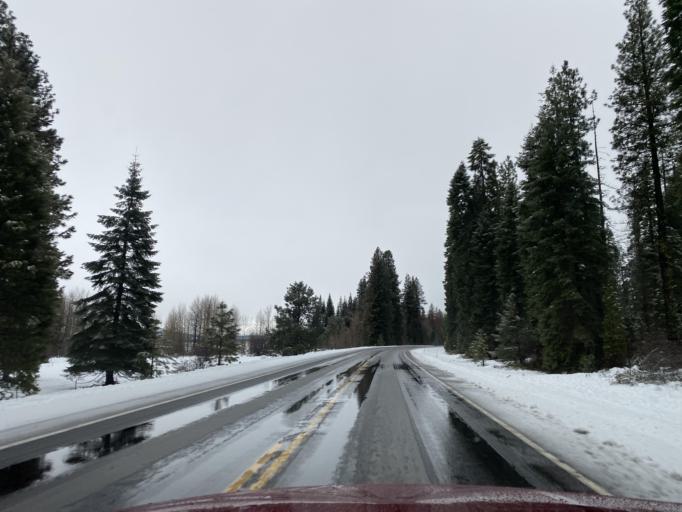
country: US
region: Oregon
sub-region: Klamath County
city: Klamath Falls
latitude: 42.5500
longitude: -122.0862
